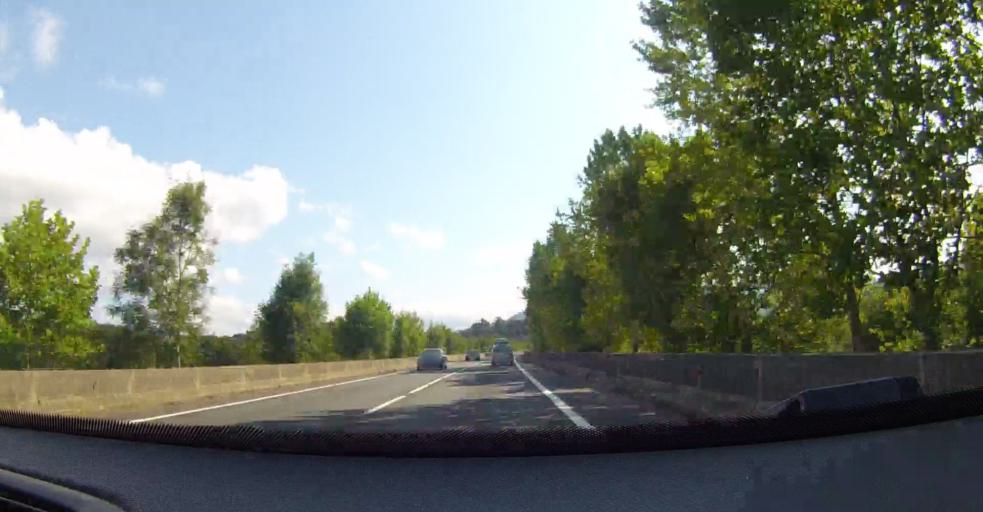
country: ES
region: Basque Country
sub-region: Bizkaia
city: Gernika-Lumo
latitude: 43.3091
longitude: -2.6737
